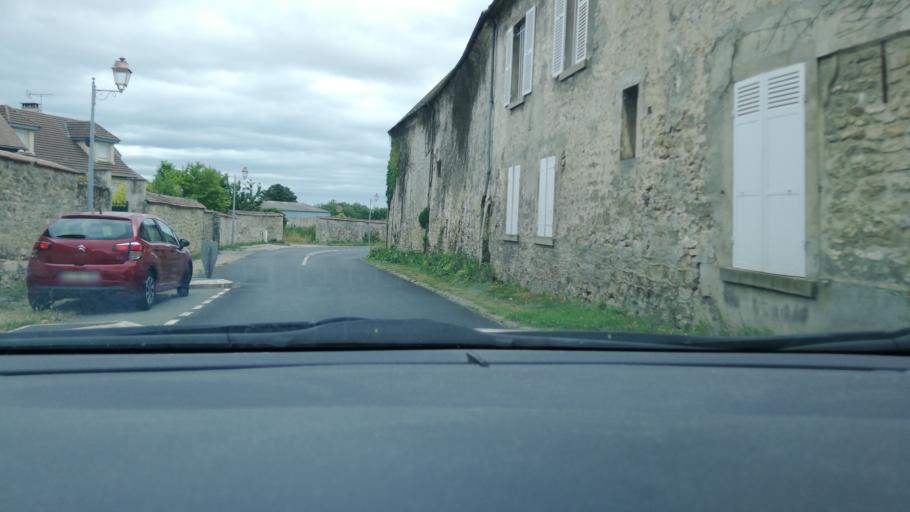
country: FR
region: Ile-de-France
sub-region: Departement du Val-d'Oise
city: Ennery
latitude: 49.1009
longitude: 2.1331
